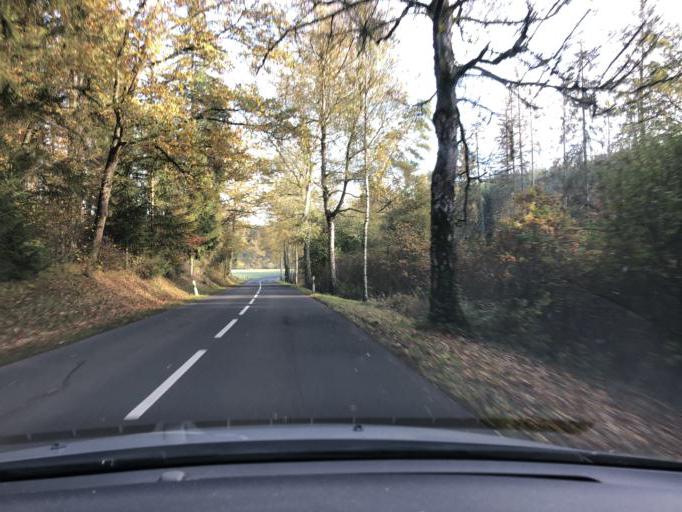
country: DE
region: Thuringia
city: Reurieth
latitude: 50.4289
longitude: 10.6323
